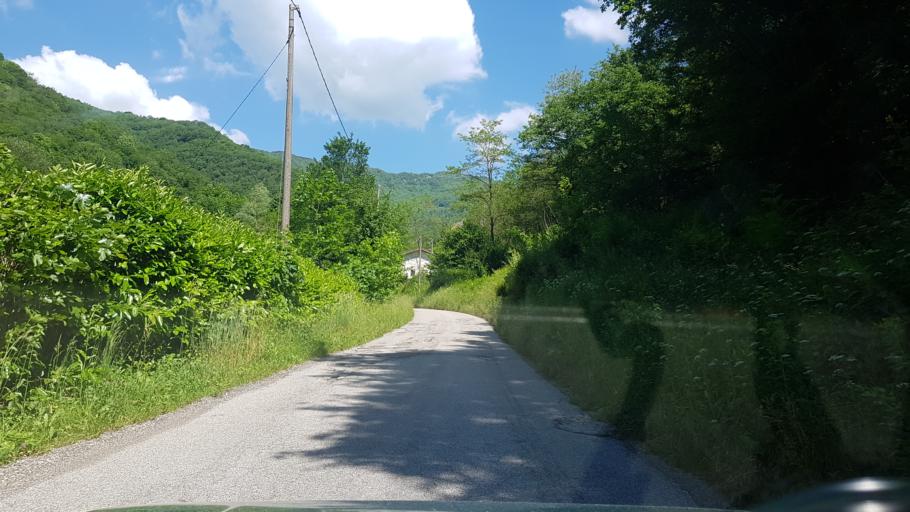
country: IT
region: Friuli Venezia Giulia
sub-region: Provincia di Udine
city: Torreano
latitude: 46.1561
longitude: 13.4322
